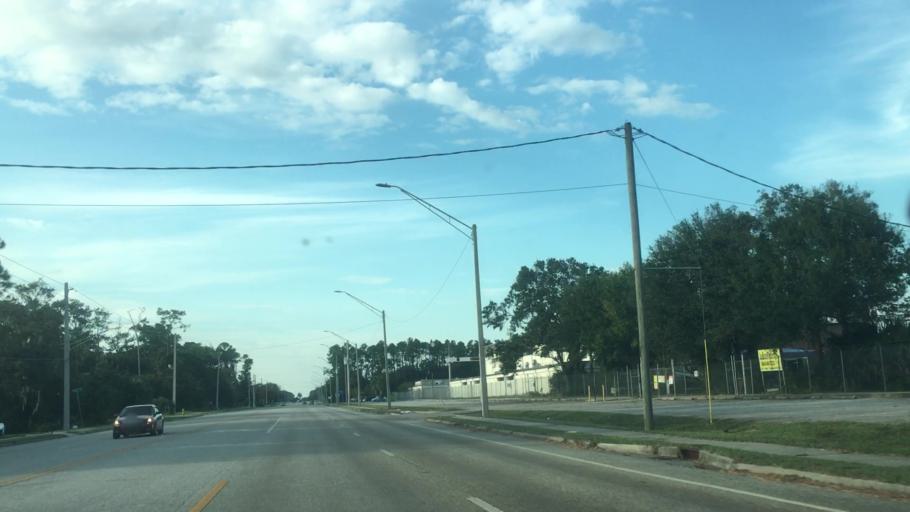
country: US
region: Florida
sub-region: Duval County
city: Atlantic Beach
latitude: 30.3295
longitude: -81.5232
